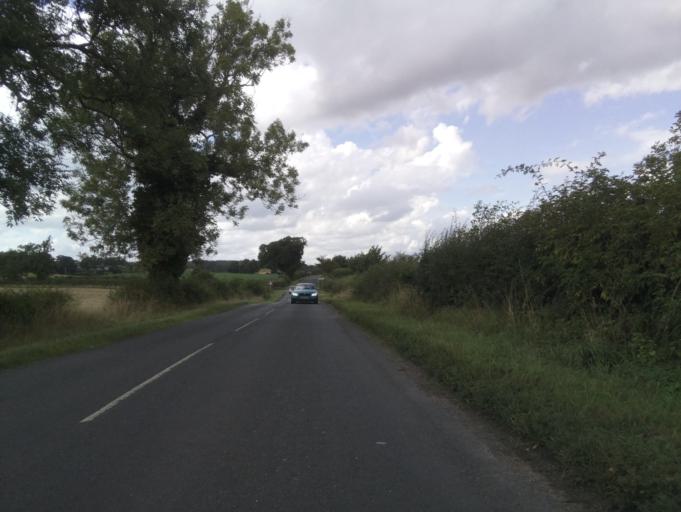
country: GB
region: England
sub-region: North Yorkshire
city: Bedale
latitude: 54.2431
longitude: -1.6888
